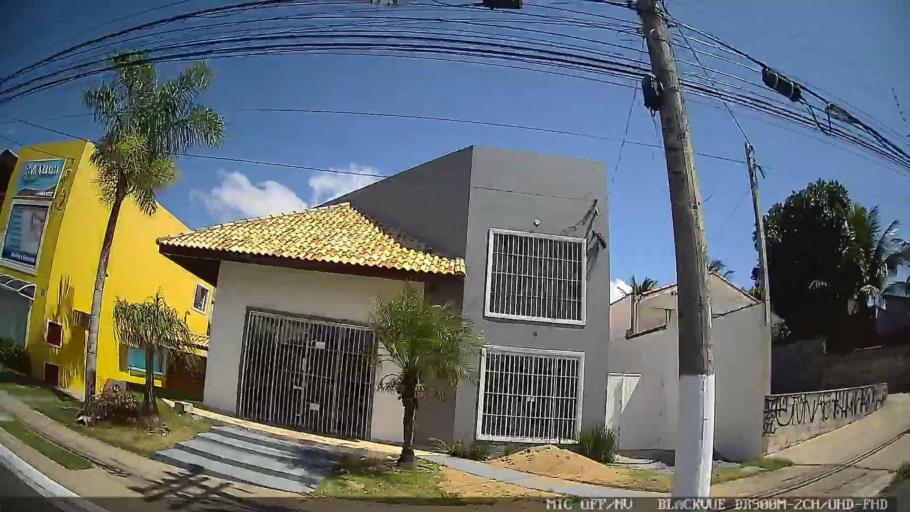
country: BR
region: Sao Paulo
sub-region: Peruibe
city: Peruibe
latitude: -24.3144
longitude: -46.9994
